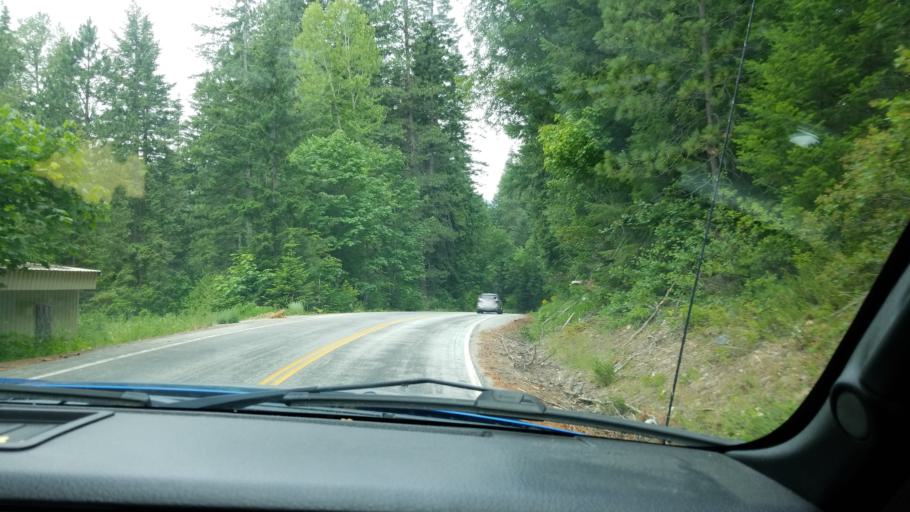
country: US
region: Washington
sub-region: Chelan County
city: Leavenworth
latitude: 47.8519
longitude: -120.8338
